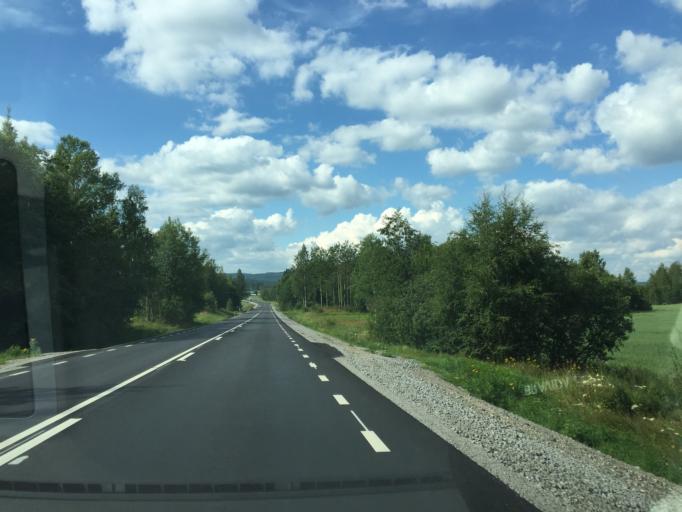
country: SE
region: Gaevleborg
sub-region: Bollnas Kommun
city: Kilafors
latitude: 61.1671
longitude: 16.8255
